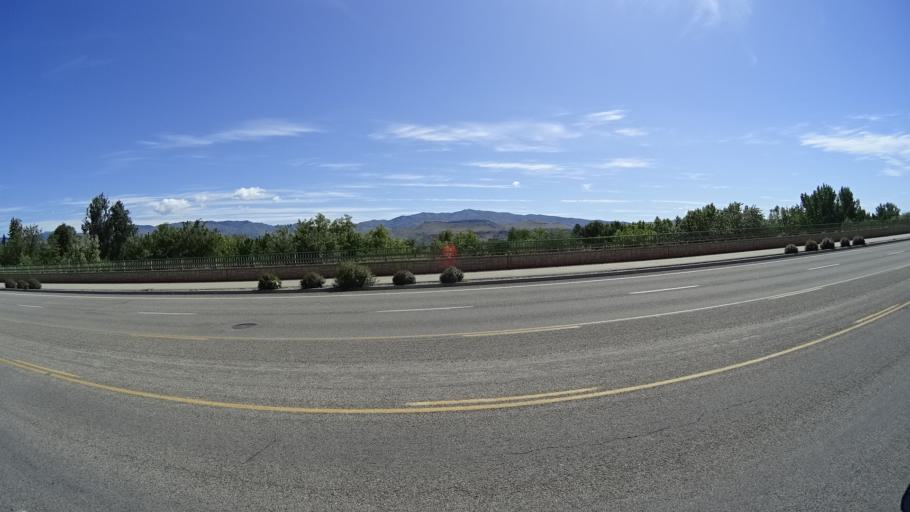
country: US
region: Idaho
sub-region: Ada County
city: Boise
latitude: 43.5879
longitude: -116.2015
